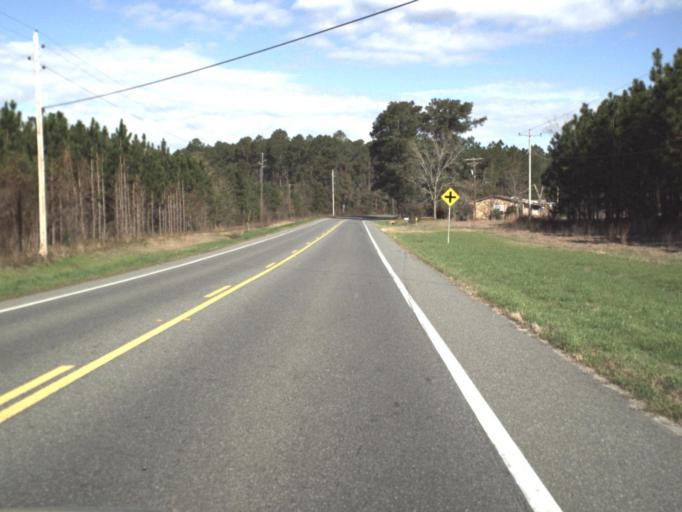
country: US
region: Florida
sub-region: Jackson County
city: Malone
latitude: 30.9295
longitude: -85.1643
